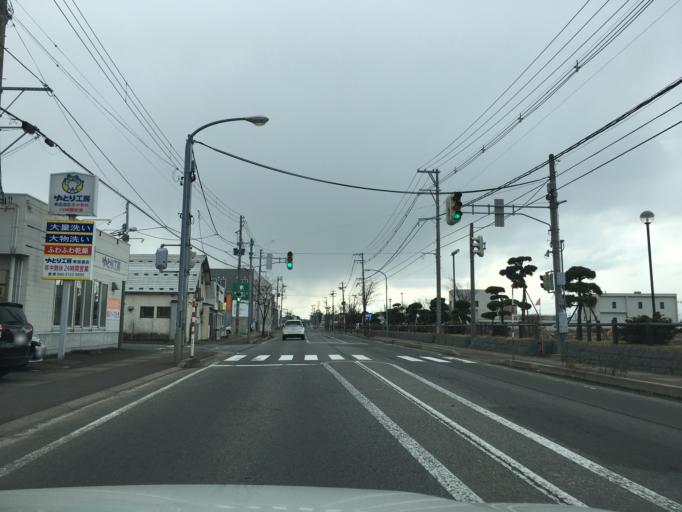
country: JP
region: Aomori
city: Aomori Shi
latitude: 40.8339
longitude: 140.7933
